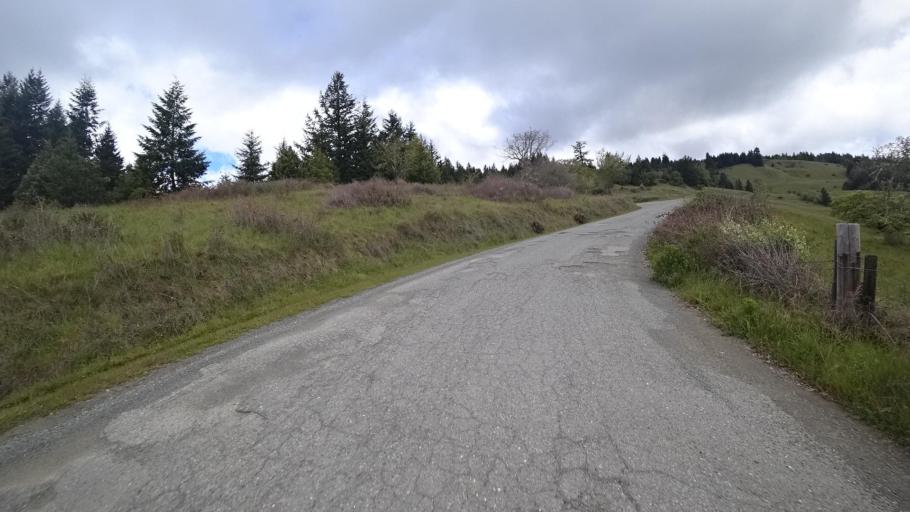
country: US
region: California
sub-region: Humboldt County
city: Blue Lake
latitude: 40.8542
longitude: -123.9182
